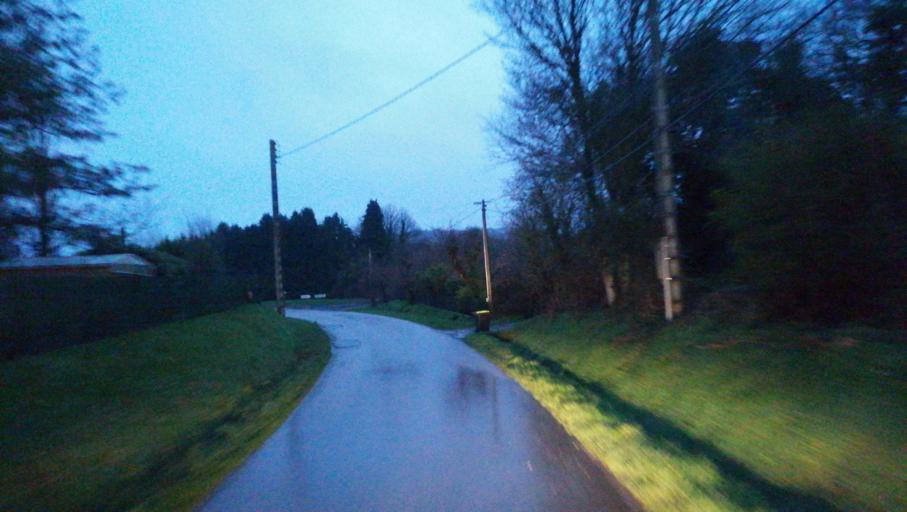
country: FR
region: Brittany
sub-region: Departement des Cotes-d'Armor
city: Plouagat
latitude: 48.4775
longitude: -2.9730
